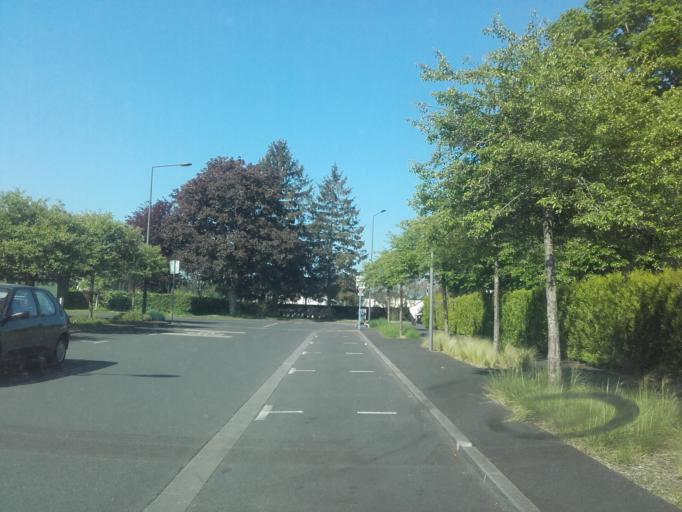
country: FR
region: Centre
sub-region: Departement d'Indre-et-Loire
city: Saint-Cyr-sur-Loire
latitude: 47.4230
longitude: 0.6795
